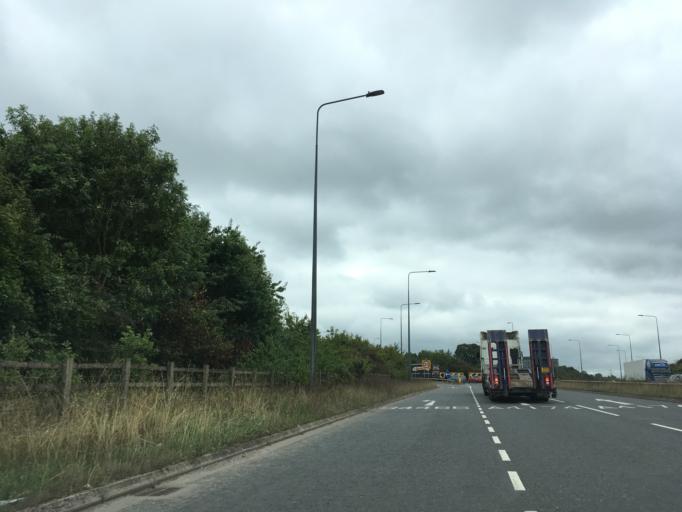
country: GB
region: England
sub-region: South Gloucestershire
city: Siston
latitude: 51.4882
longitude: -2.4694
